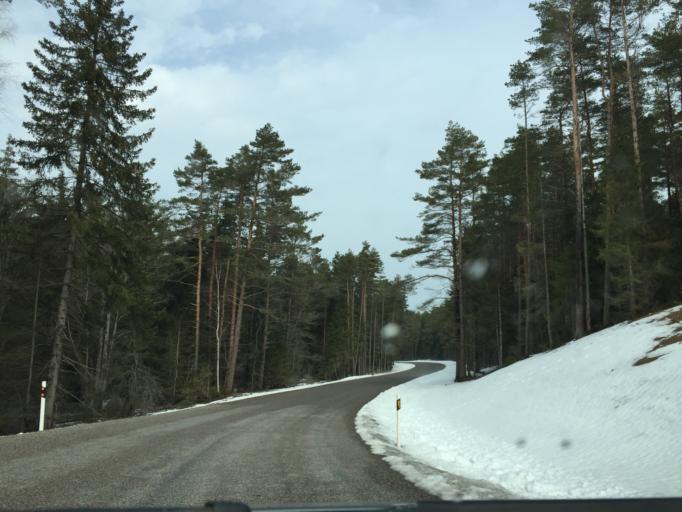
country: EE
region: Saare
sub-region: Kuressaare linn
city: Kuressaare
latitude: 58.4001
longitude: 22.1718
